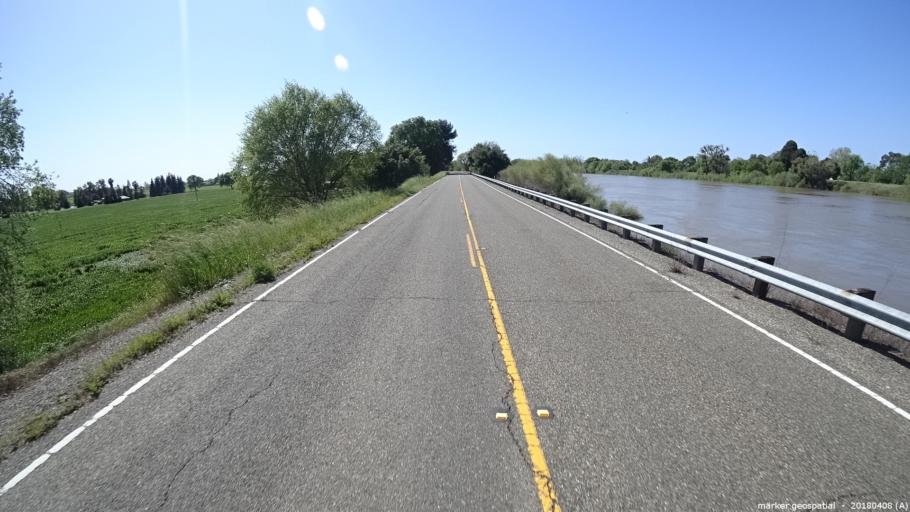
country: US
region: California
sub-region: Sacramento County
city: Parkway
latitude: 38.4340
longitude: -121.5216
